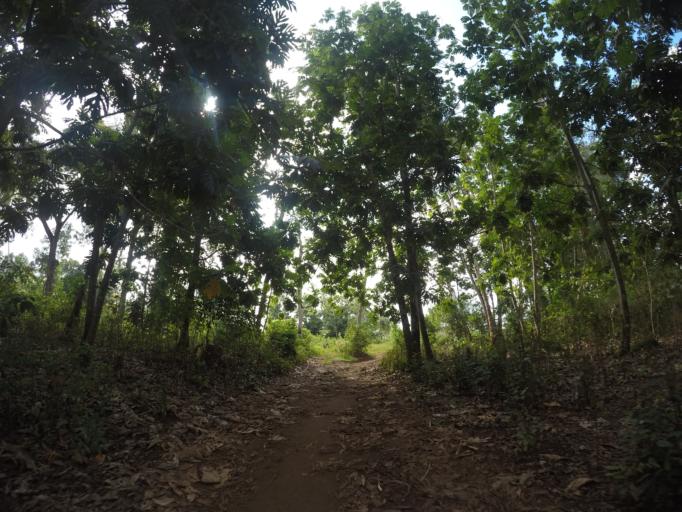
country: TZ
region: Zanzibar Central/South
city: Koani
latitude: -6.1888
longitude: 39.3243
